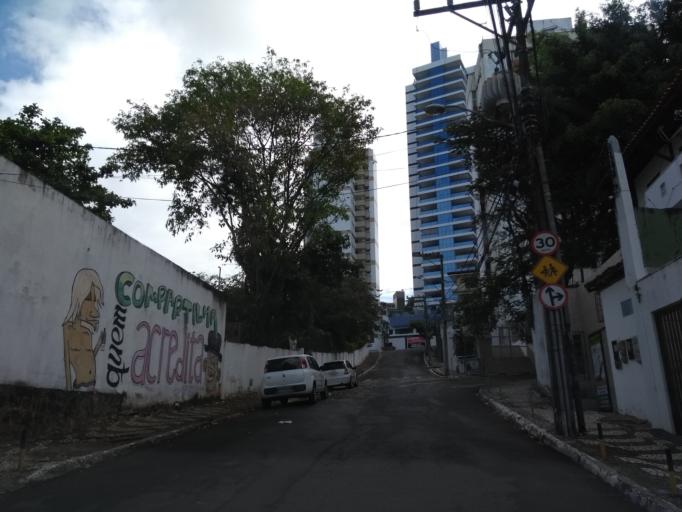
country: BR
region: Bahia
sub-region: Salvador
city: Salvador
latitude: -13.0032
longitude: -38.5180
